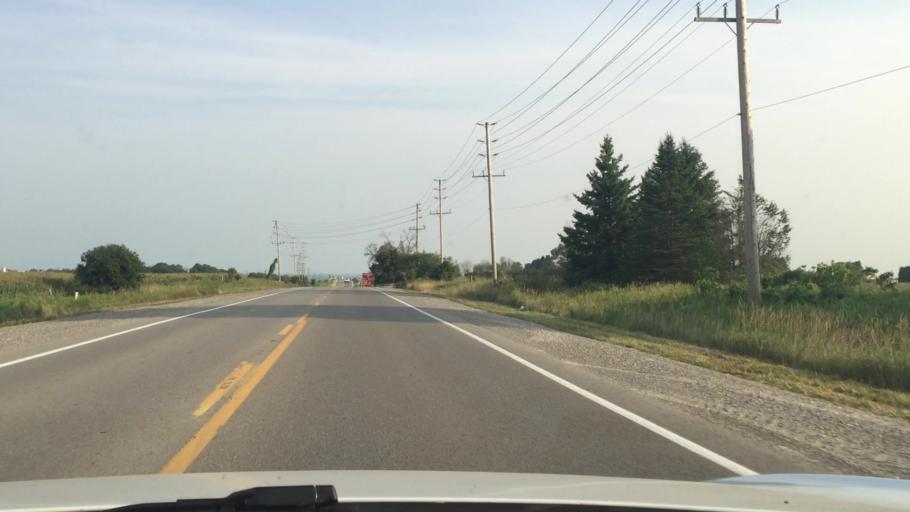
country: CA
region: Ontario
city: Oshawa
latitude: 43.8883
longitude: -78.7678
